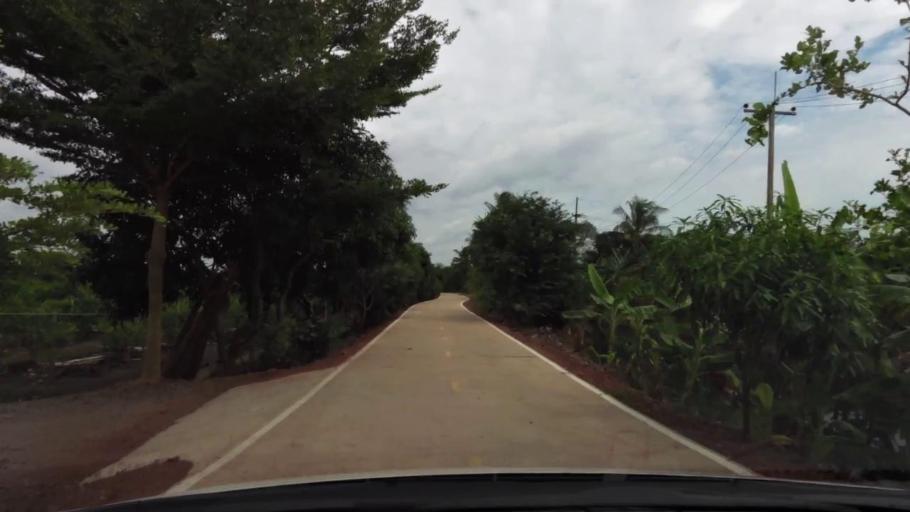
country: TH
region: Ratchaburi
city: Damnoen Saduak
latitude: 13.5566
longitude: 99.9804
